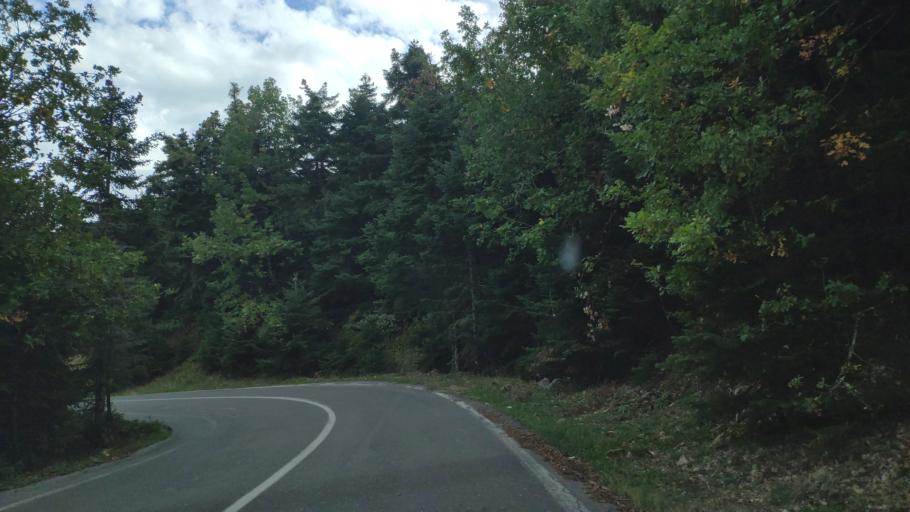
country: GR
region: Central Greece
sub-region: Nomos Fthiotidos
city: Anthili
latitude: 38.7372
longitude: 22.3749
